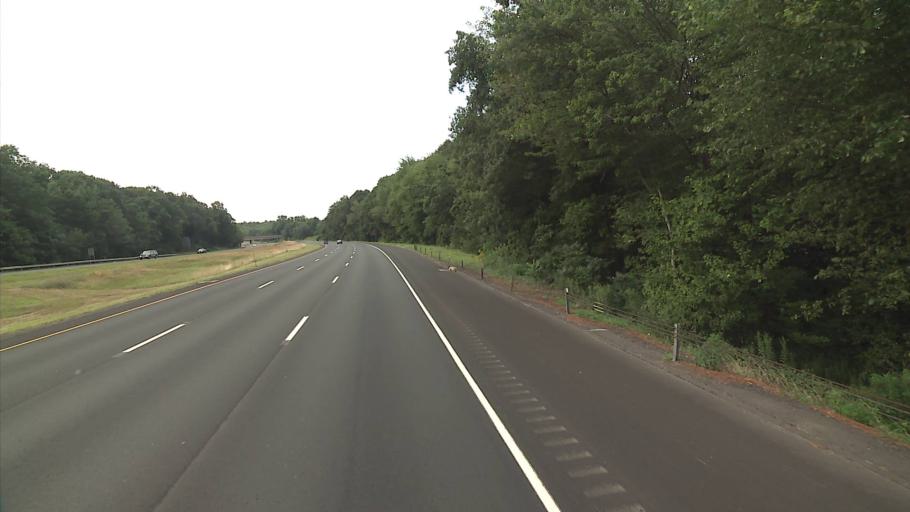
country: US
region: Connecticut
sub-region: New Haven County
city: Wolcott
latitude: 41.5968
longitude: -72.9036
